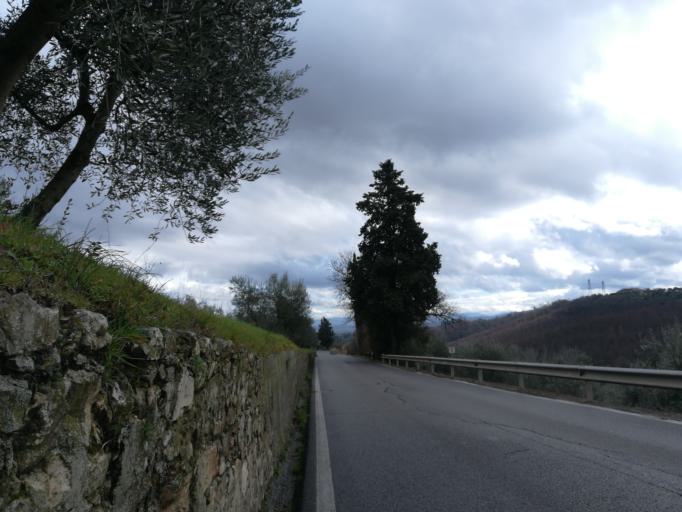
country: IT
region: Tuscany
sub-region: Provincia di Prato
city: Poggio A Caiano
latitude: 43.8043
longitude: 11.0346
